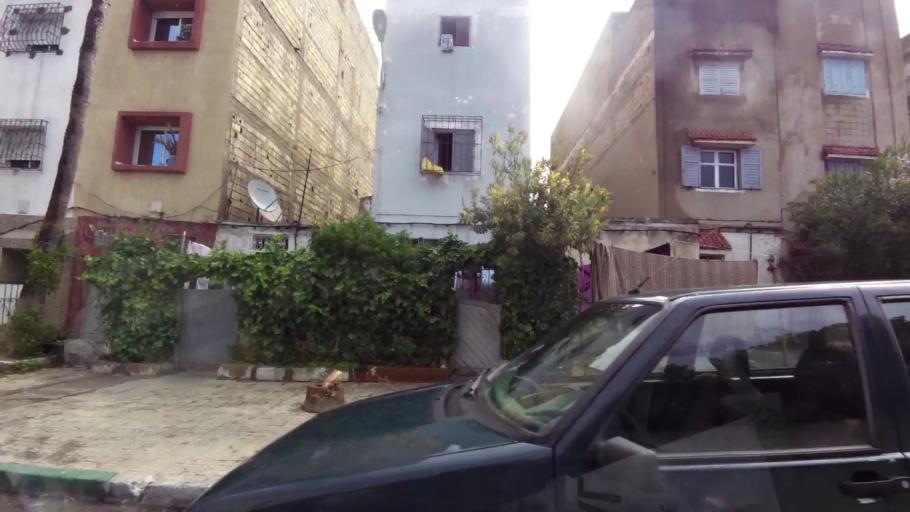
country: MA
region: Grand Casablanca
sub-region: Casablanca
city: Casablanca
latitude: 33.5754
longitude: -7.6735
